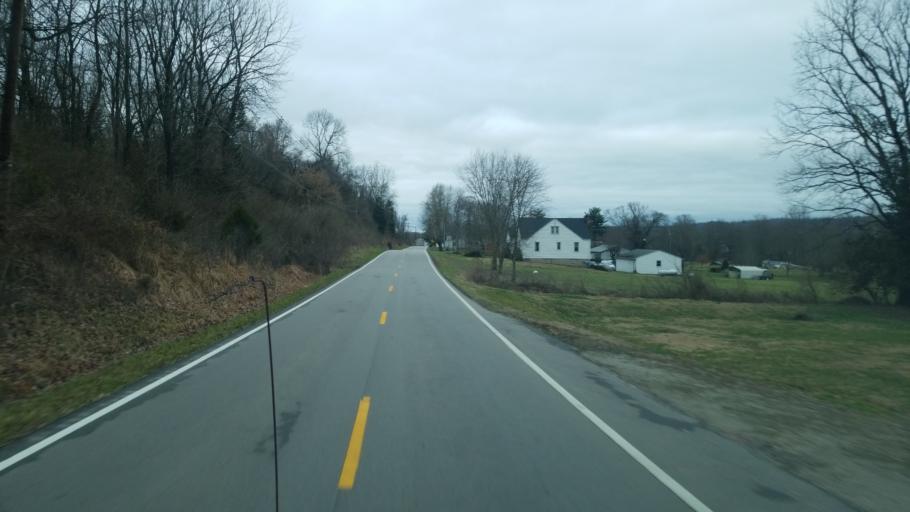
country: US
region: Ohio
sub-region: Clermont County
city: New Richmond
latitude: 38.8825
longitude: -84.2440
